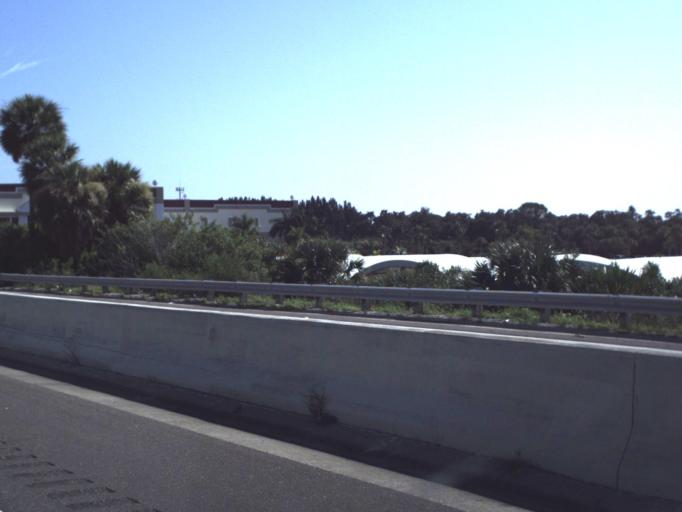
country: US
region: Florida
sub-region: Pinellas County
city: Gulfport
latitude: 27.7128
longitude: -82.6793
